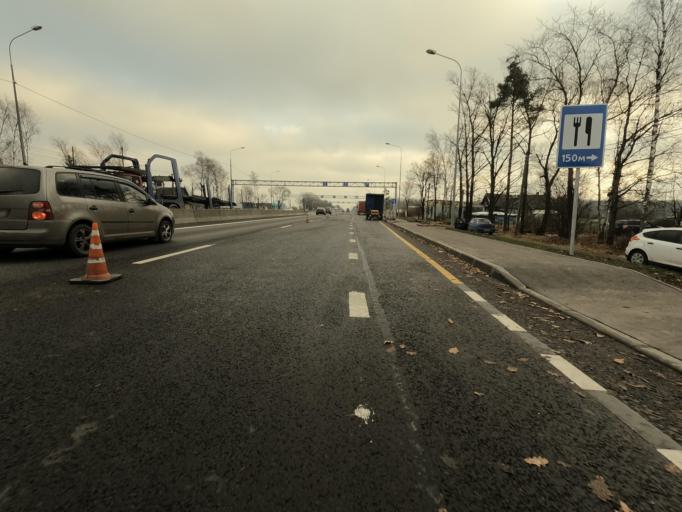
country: RU
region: Leningrad
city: Mga
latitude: 59.7257
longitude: 31.0947
